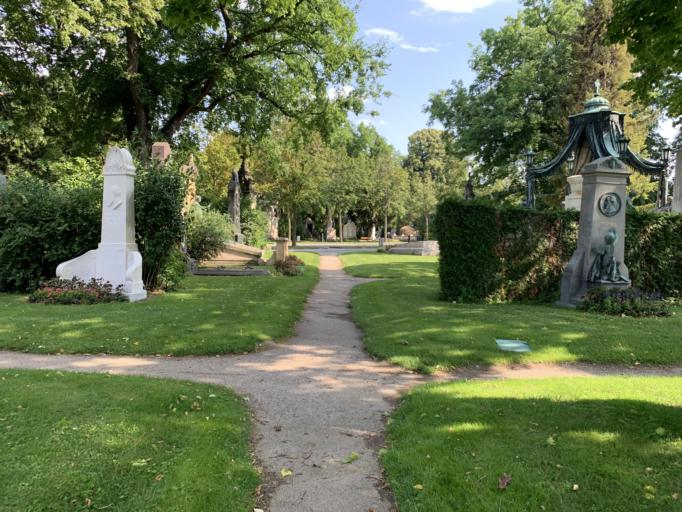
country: AT
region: Lower Austria
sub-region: Politischer Bezirk Wien-Umgebung
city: Schwechat
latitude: 48.1526
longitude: 16.4393
